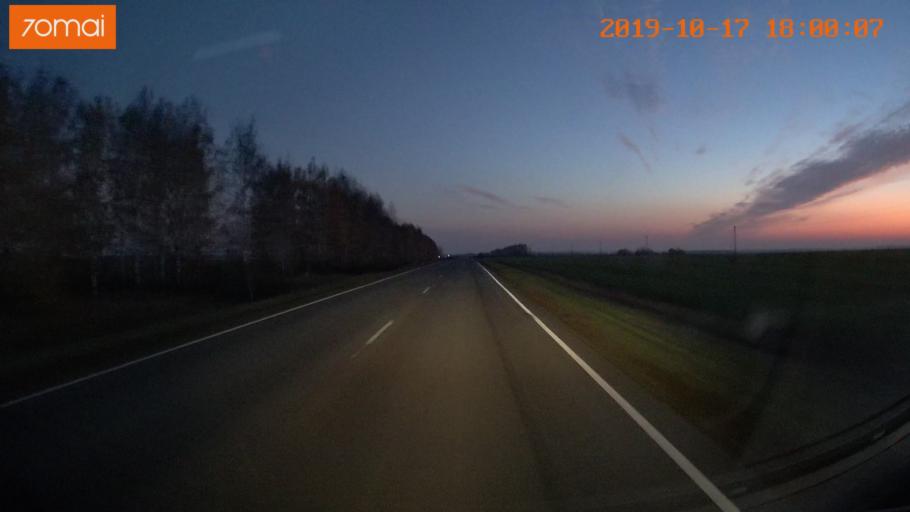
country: RU
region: Tula
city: Kurkino
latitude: 53.5266
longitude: 38.6174
